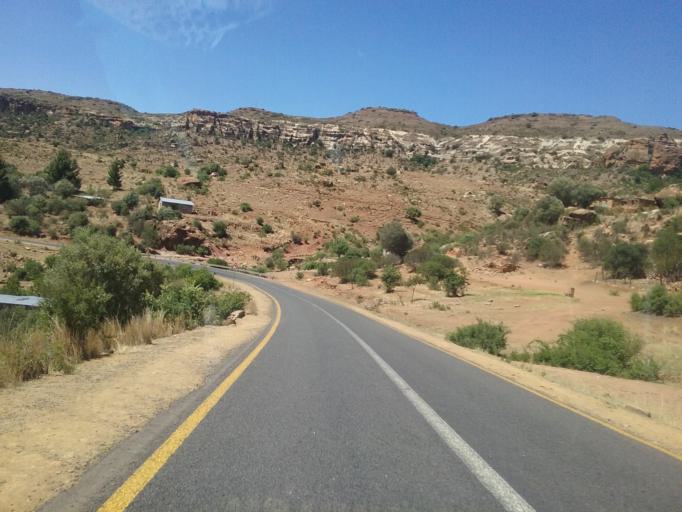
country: LS
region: Quthing
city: Quthing
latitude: -30.2915
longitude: 27.7605
